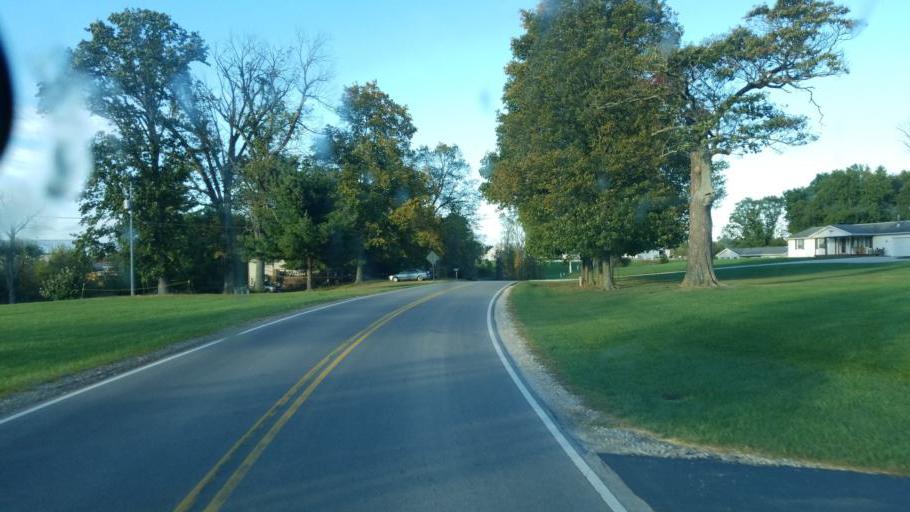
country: US
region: Ohio
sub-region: Licking County
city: Pataskala
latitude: 40.0493
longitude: -82.7333
